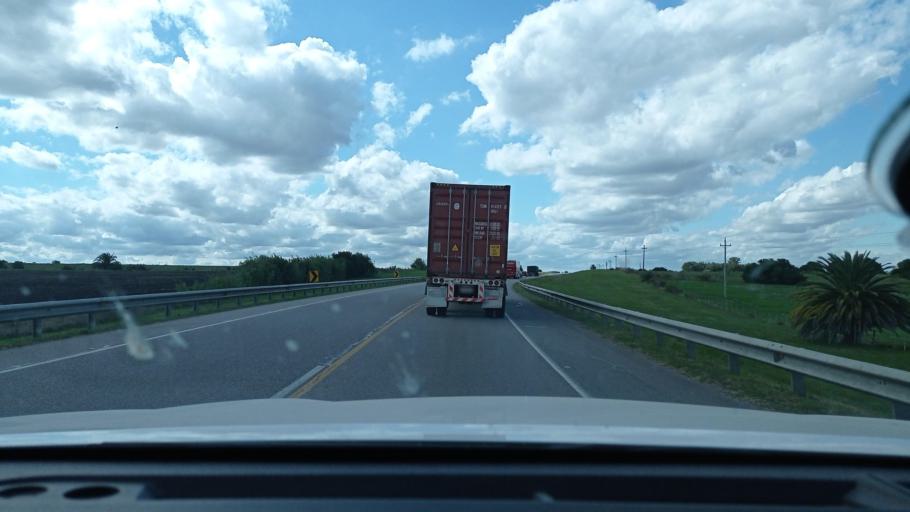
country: UY
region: Florida
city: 25 de Mayo
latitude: -34.2325
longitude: -56.2119
